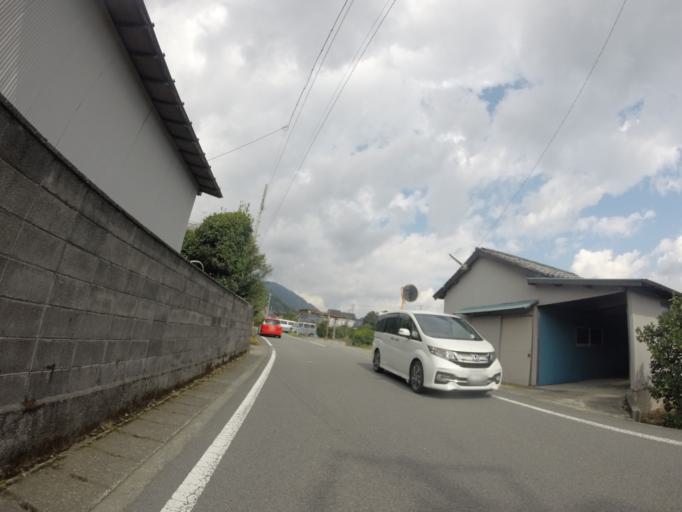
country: JP
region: Shizuoka
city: Shizuoka-shi
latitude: 35.0537
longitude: 138.4760
